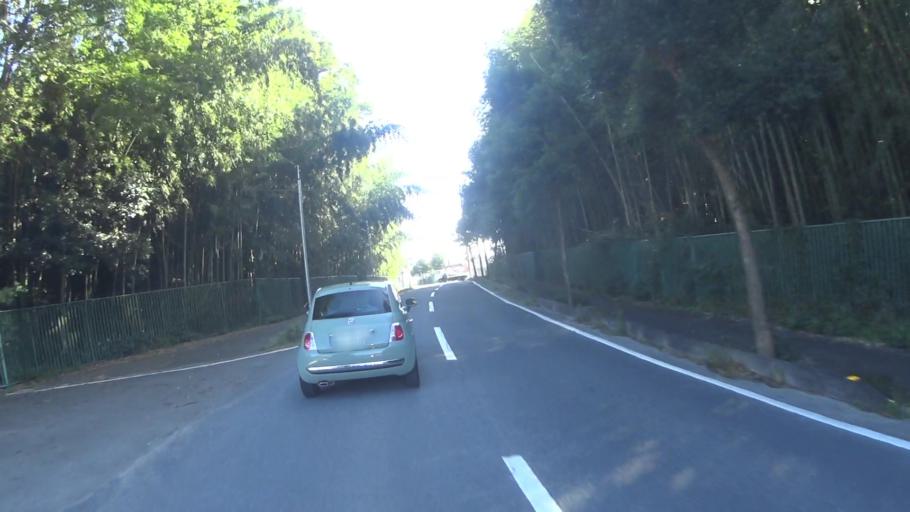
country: JP
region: Kyoto
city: Kameoka
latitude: 35.0281
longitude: 135.5876
